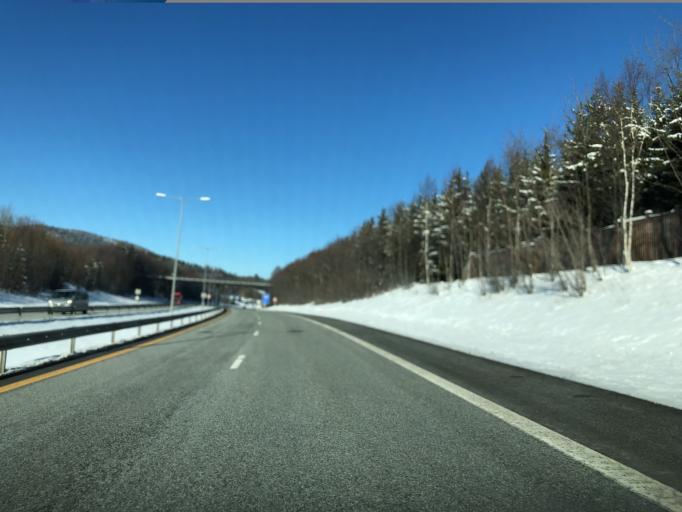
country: NO
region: Buskerud
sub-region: Drammen
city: Skoger
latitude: 59.6817
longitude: 10.2462
